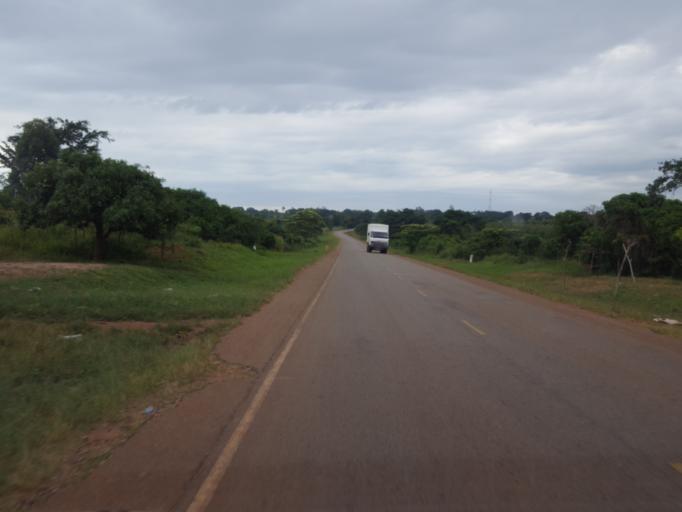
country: UG
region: Central Region
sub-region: Kiboga District
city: Kiboga
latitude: 1.0206
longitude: 31.6865
